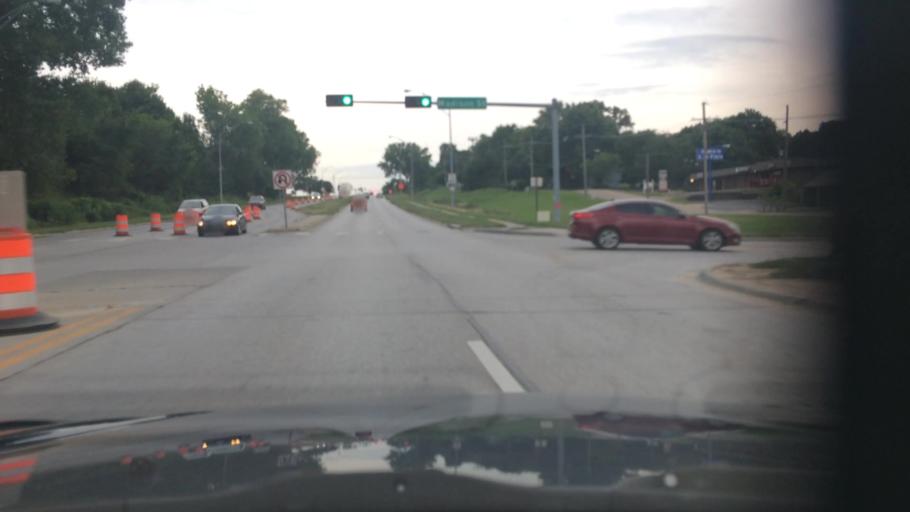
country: US
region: Nebraska
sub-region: Douglas County
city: Ralston
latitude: 41.1959
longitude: -96.0431
